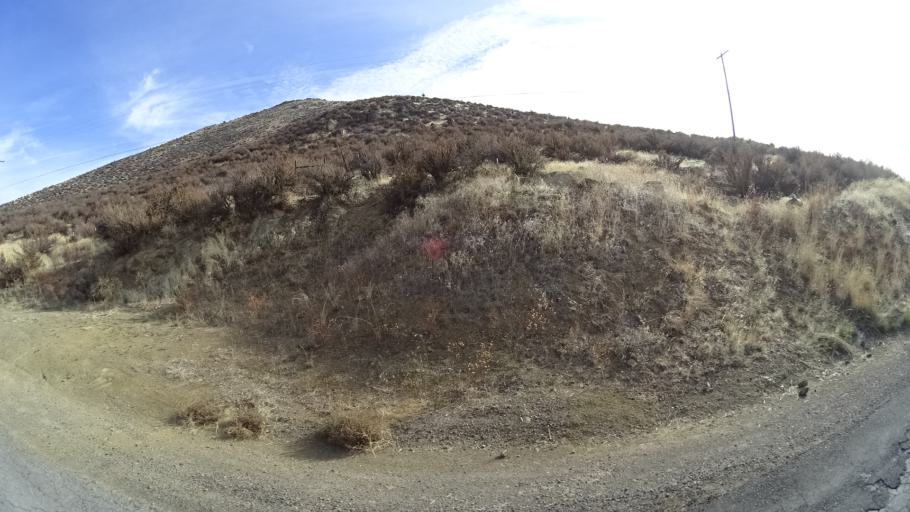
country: US
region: California
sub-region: Siskiyou County
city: Montague
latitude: 41.7129
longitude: -122.5217
